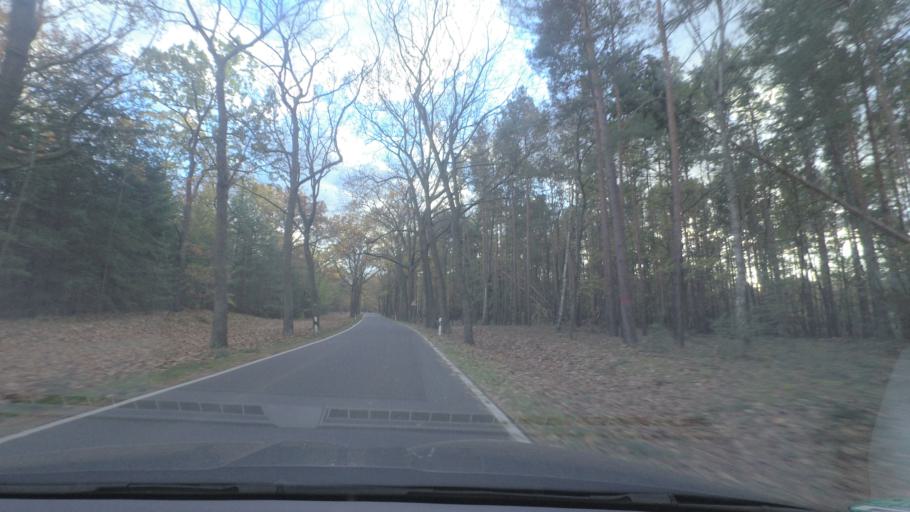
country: DE
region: Brandenburg
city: Sperenberg
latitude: 52.0173
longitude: 13.3181
